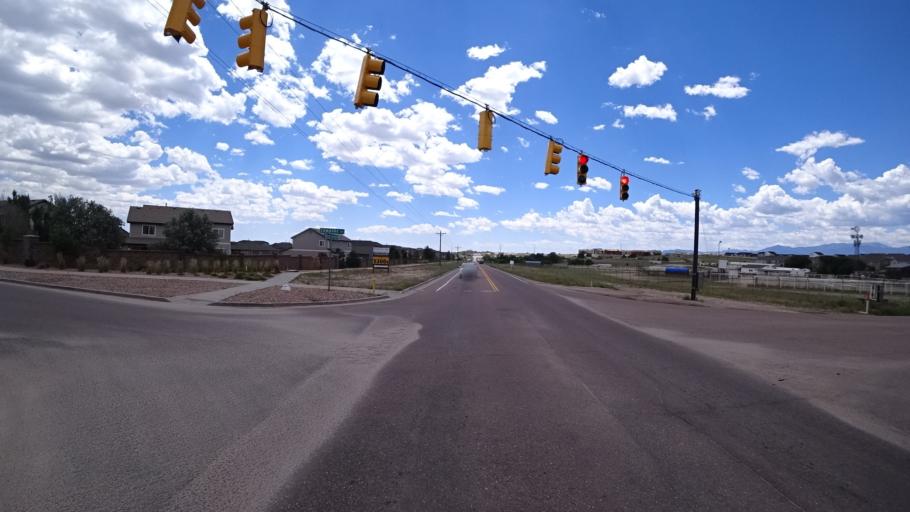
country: US
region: Colorado
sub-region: El Paso County
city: Black Forest
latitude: 38.9515
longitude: -104.7007
